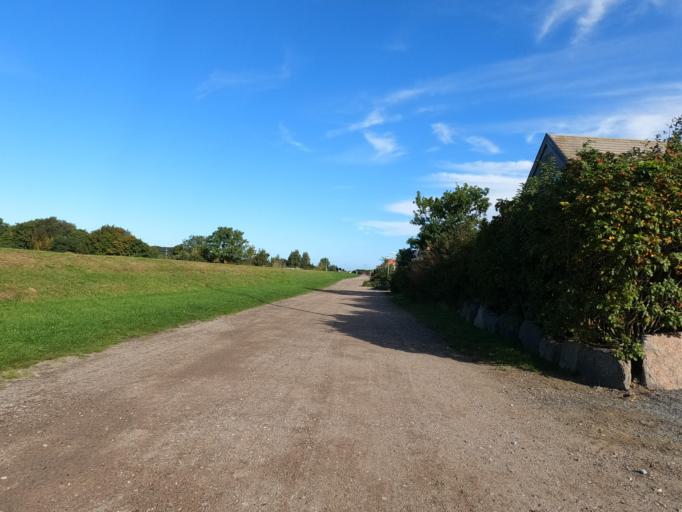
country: DE
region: Schleswig-Holstein
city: Dahme
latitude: 54.2728
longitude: 11.0830
